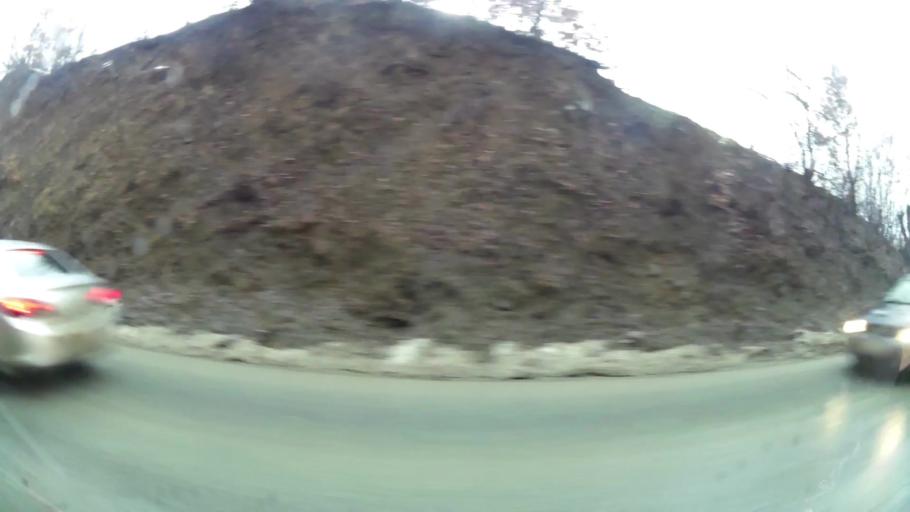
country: XK
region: Ferizaj
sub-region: Hani i Elezit
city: Hani i Elezit
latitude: 42.1763
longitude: 21.2685
